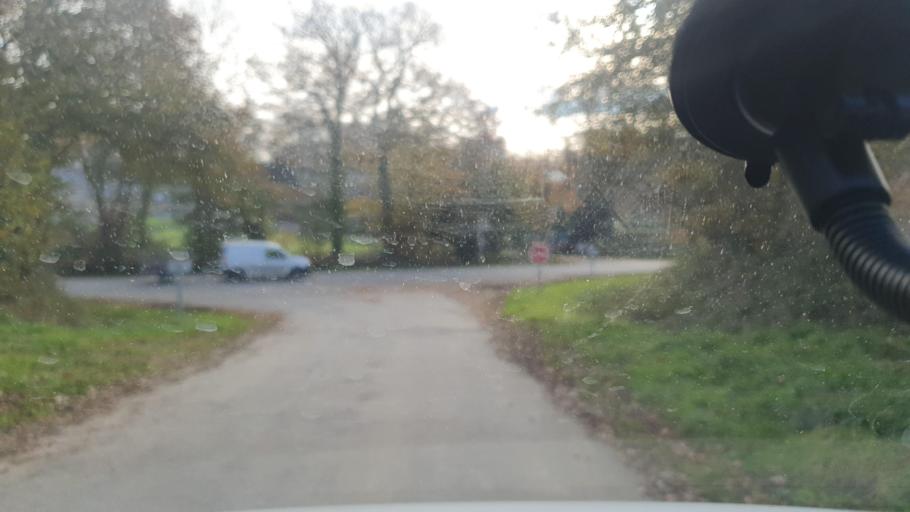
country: FR
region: Brittany
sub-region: Departement du Finistere
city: Landrevarzec
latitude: 48.0996
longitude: -4.0340
